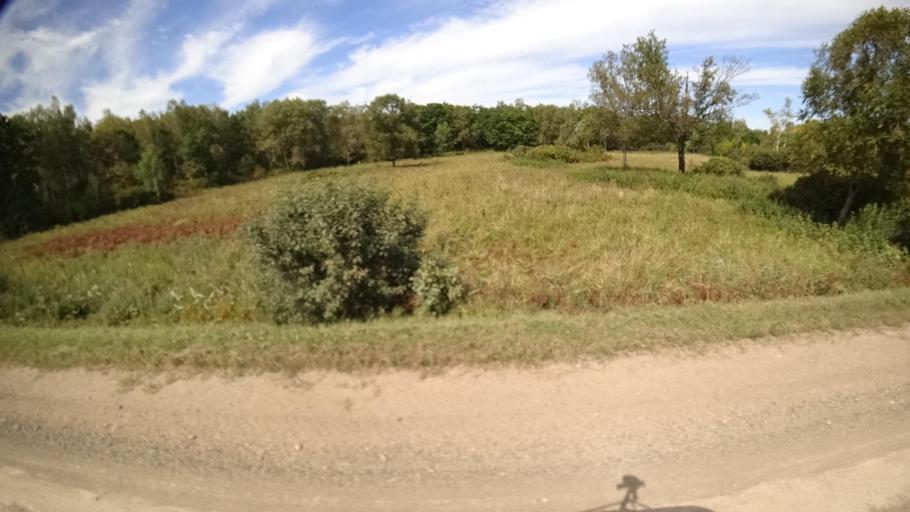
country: RU
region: Primorskiy
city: Yakovlevka
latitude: 44.6986
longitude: 133.6267
